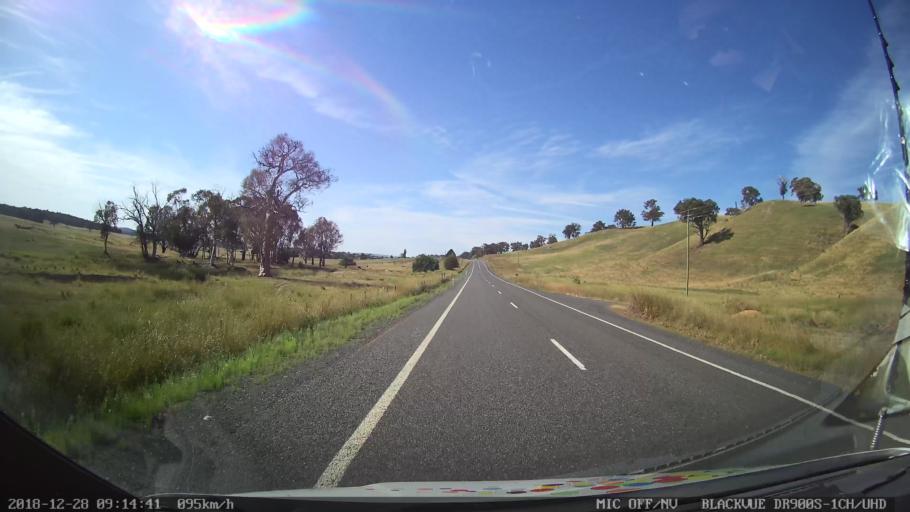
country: AU
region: New South Wales
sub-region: Upper Lachlan Shire
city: Crookwell
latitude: -34.2858
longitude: 149.3462
